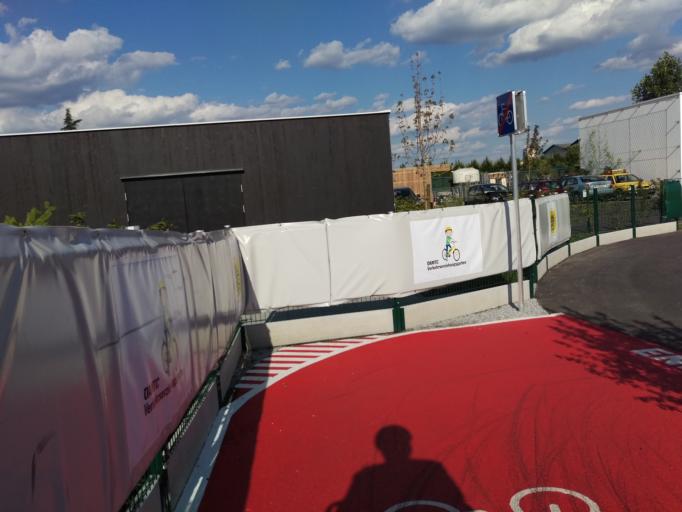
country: AT
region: Styria
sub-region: Graz Stadt
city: Wetzelsdorf
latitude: 47.0664
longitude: 15.4134
